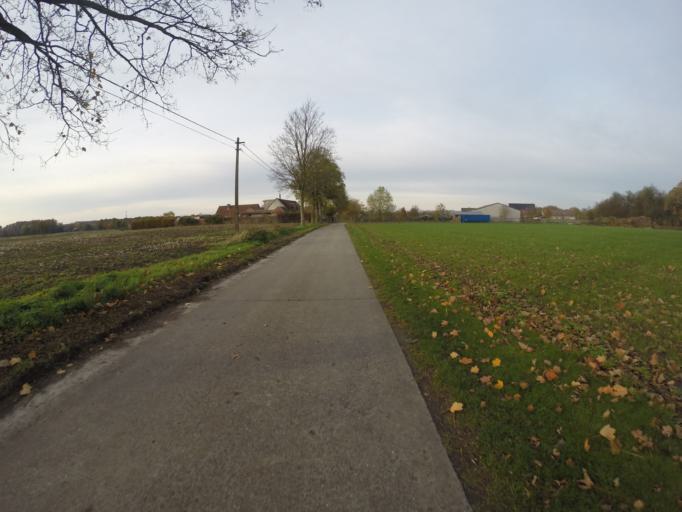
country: BE
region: Flanders
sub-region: Provincie Oost-Vlaanderen
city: Nevele
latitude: 51.0697
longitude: 3.5049
